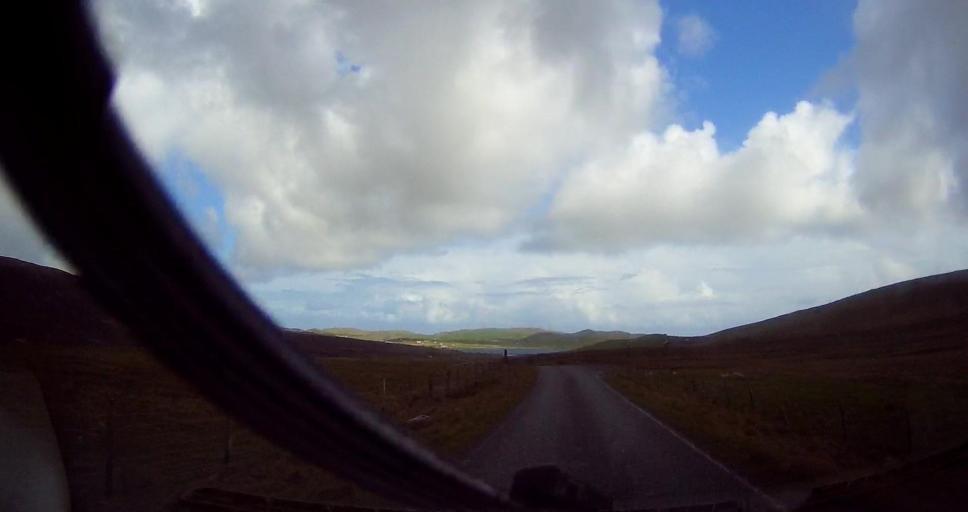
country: GB
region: Scotland
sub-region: Shetland Islands
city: Lerwick
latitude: 60.5620
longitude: -1.3350
